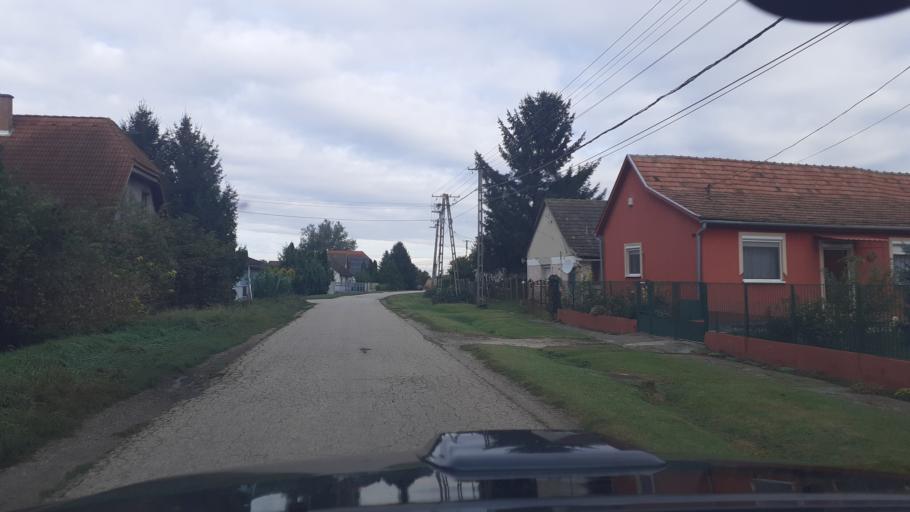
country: HU
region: Fejer
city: Baracs
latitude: 46.9213
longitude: 18.8770
